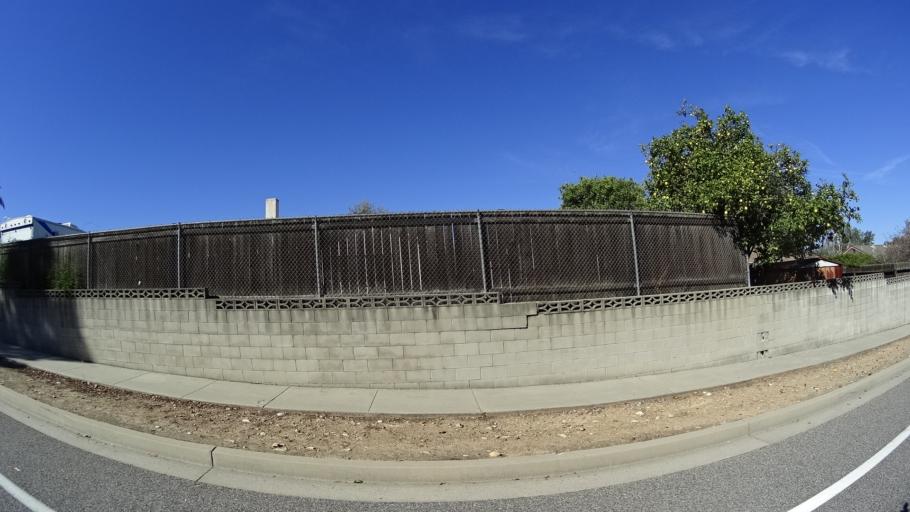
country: US
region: California
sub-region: Ventura County
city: Thousand Oaks
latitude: 34.2216
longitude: -118.8567
